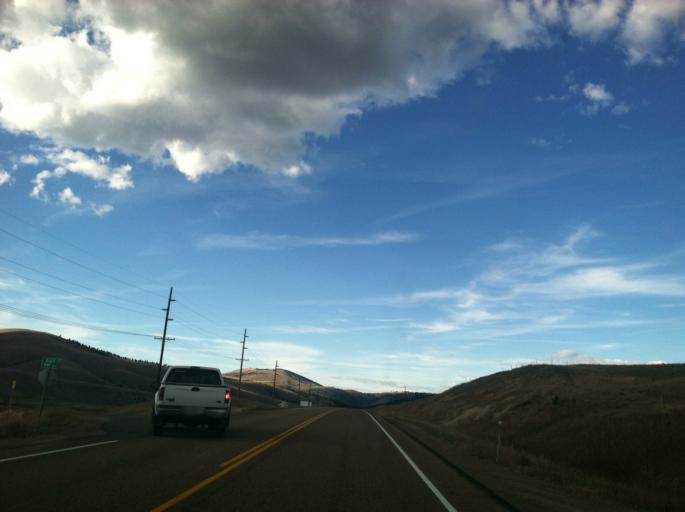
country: US
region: Montana
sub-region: Granite County
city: Philipsburg
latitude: 46.3651
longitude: -113.3143
